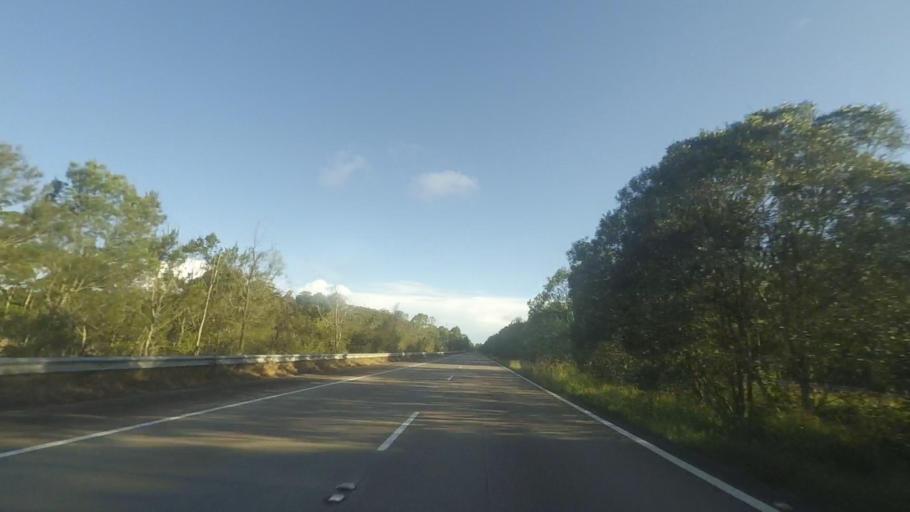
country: AU
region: New South Wales
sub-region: Great Lakes
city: Bulahdelah
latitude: -32.2910
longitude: 152.3426
